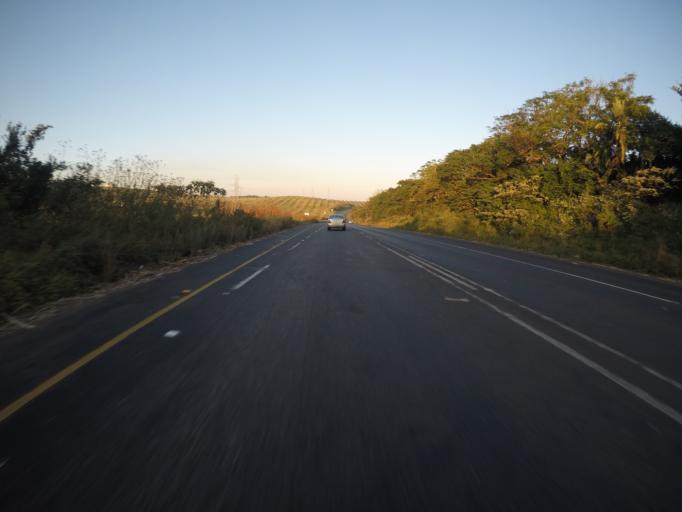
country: ZA
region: KwaZulu-Natal
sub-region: uThungulu District Municipality
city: eSikhawini
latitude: -28.8176
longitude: 31.8864
